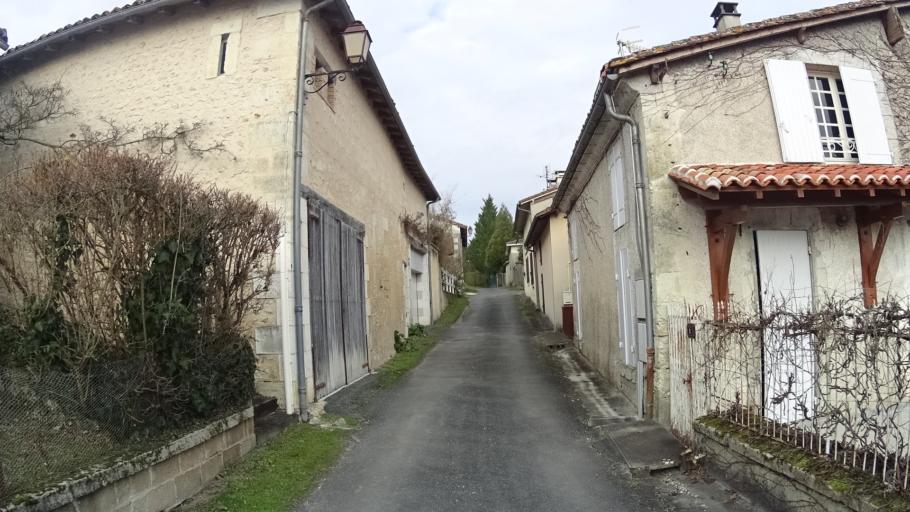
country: FR
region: Aquitaine
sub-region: Departement de la Dordogne
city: Saint-Aulaye
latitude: 45.2425
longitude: 0.1497
